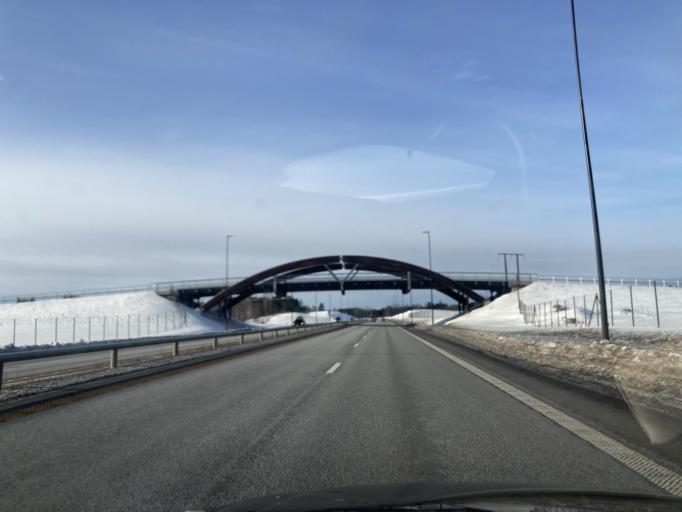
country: NO
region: Hedmark
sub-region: Loten
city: Loten
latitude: 60.8383
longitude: 11.3252
